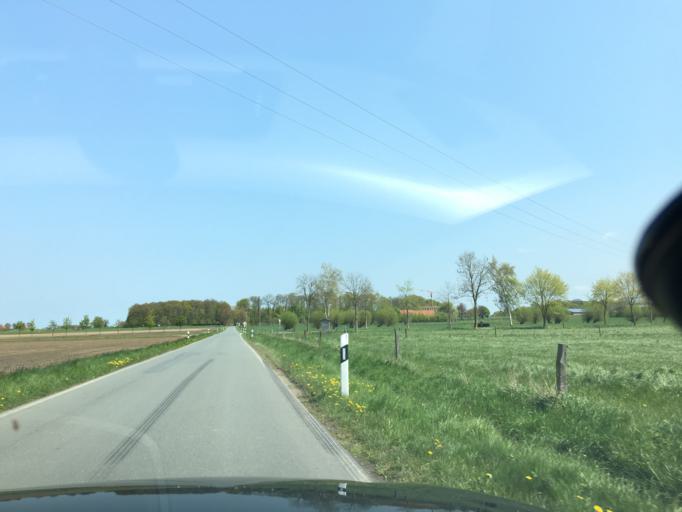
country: DE
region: North Rhine-Westphalia
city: Ludinghausen
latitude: 51.8116
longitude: 7.4664
